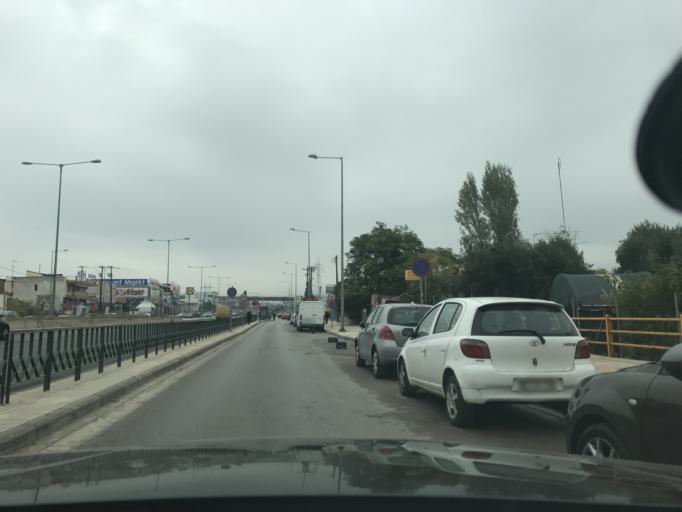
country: GR
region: Central Macedonia
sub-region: Nomos Thessalonikis
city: Stavroupoli
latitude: 40.6732
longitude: 22.9391
